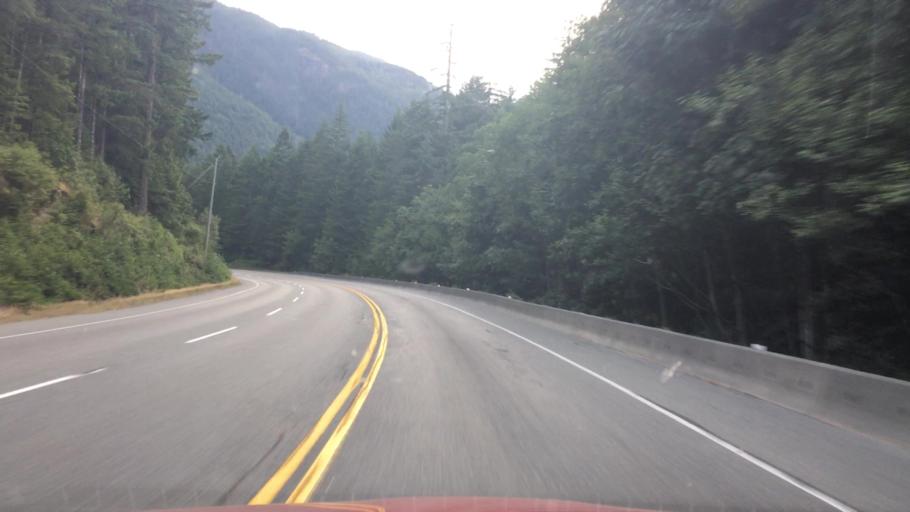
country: CA
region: British Columbia
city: Port Alberni
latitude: 49.2931
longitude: -124.5725
